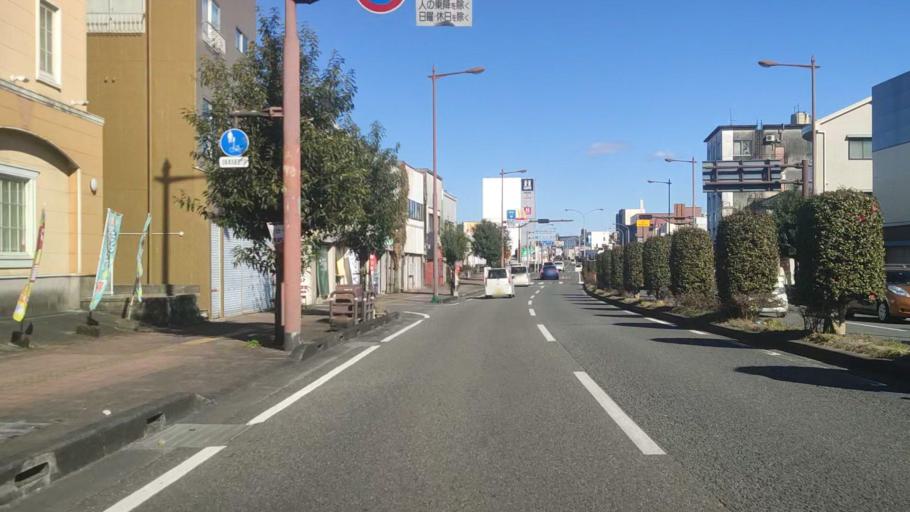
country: JP
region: Miyazaki
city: Miyakonojo
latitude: 31.7275
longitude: 131.0653
